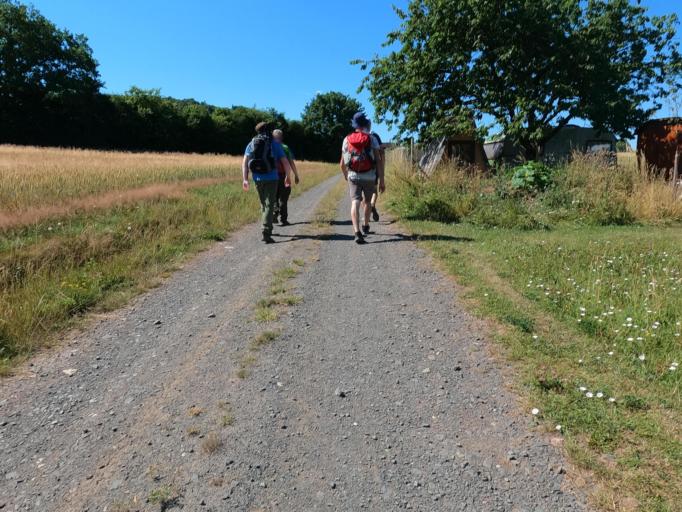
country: DE
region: Hesse
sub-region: Regierungsbezirk Darmstadt
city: Schluchtern
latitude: 50.3123
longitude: 9.5107
